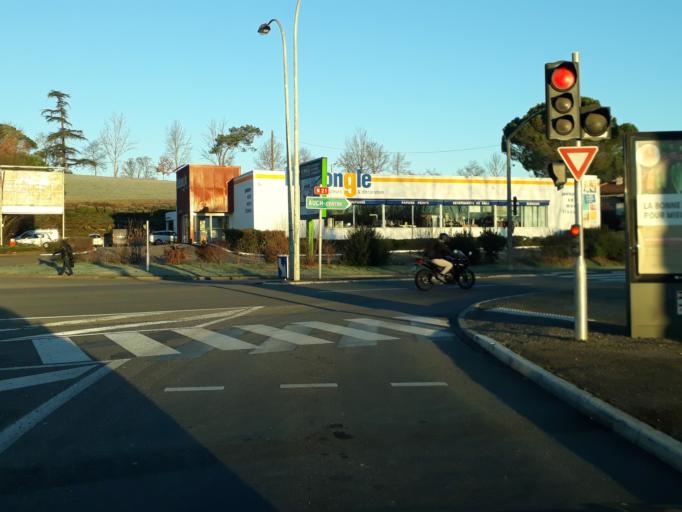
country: FR
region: Midi-Pyrenees
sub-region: Departement du Gers
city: Auch
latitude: 43.6312
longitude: 0.5816
